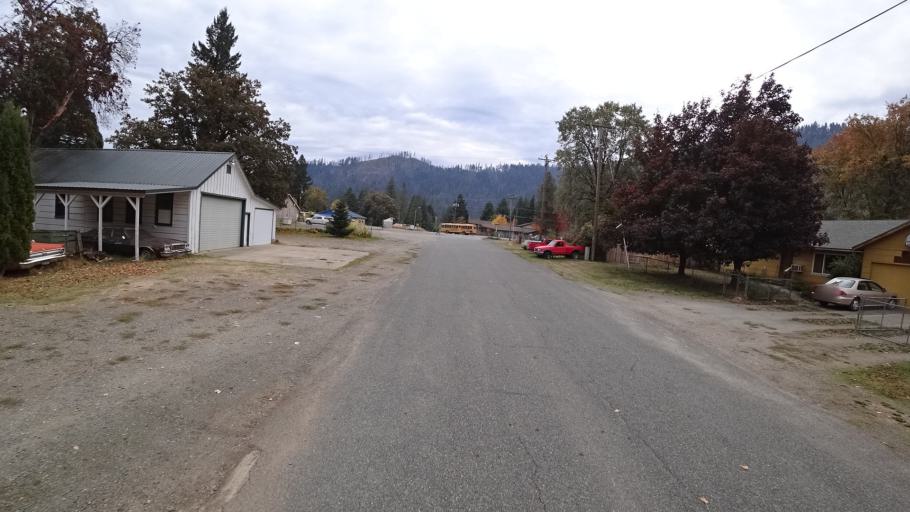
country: US
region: California
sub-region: Siskiyou County
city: Happy Camp
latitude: 41.7971
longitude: -123.3764
